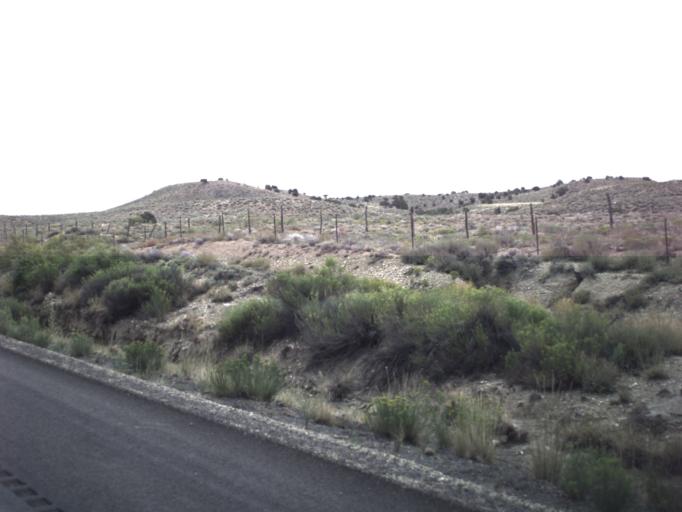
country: US
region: Utah
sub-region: Carbon County
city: Wellington
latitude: 39.5502
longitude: -110.6628
